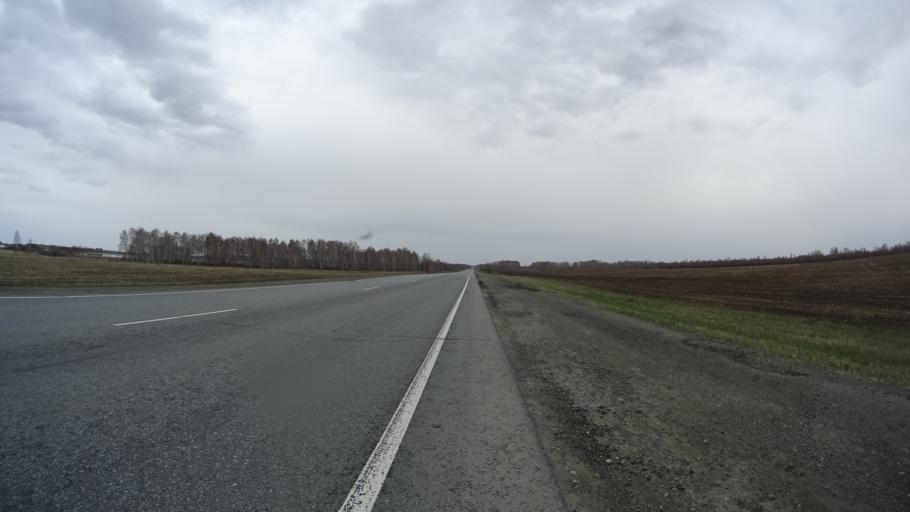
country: RU
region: Chelyabinsk
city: Krasnogorskiy
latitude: 54.6620
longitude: 61.2544
